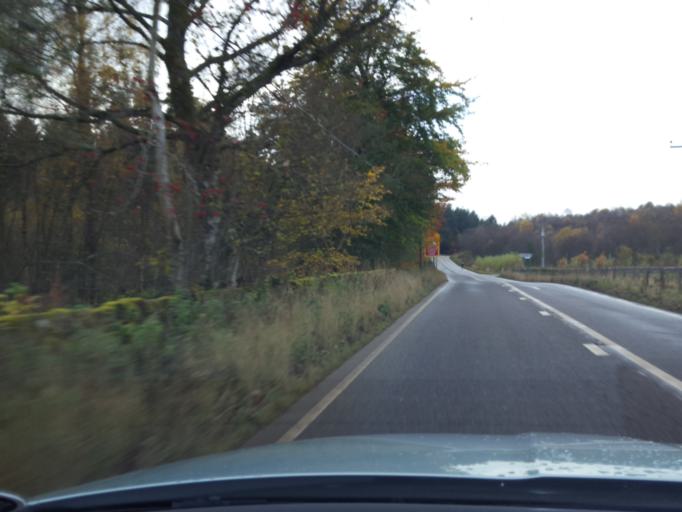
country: GB
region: Scotland
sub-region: South Lanarkshire
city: Carnwath
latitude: 55.7128
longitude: -3.5949
